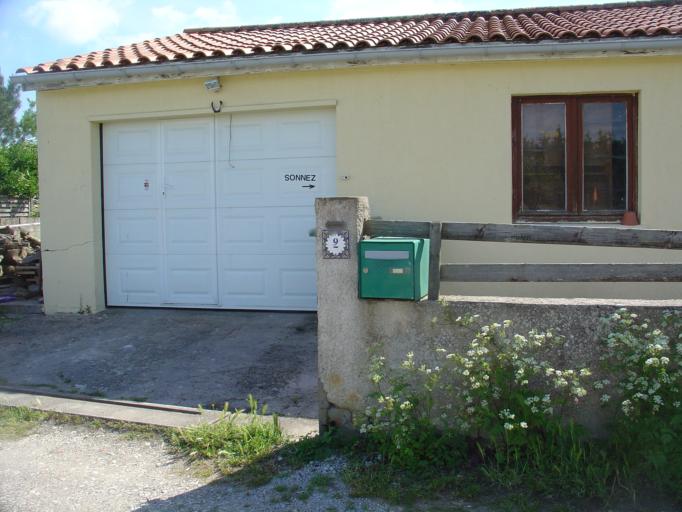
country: FR
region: Poitou-Charentes
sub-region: Departement de la Charente-Maritime
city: Dolus-d'Oleron
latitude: 45.9400
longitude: -1.2726
